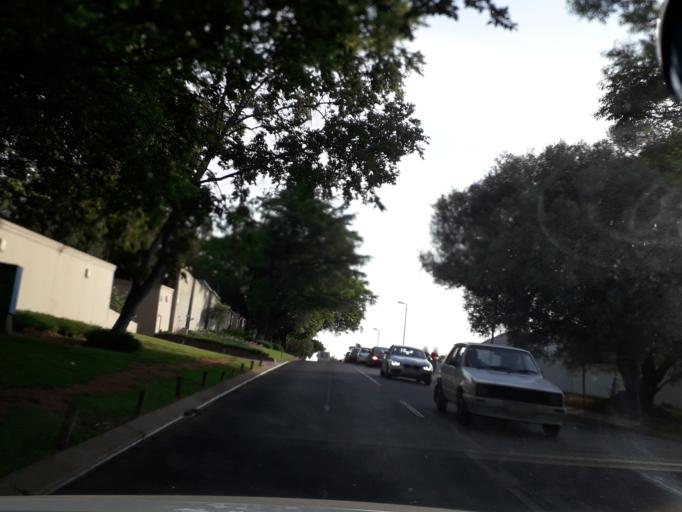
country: ZA
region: Gauteng
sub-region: City of Johannesburg Metropolitan Municipality
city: Diepsloot
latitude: -26.0668
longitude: 27.9883
